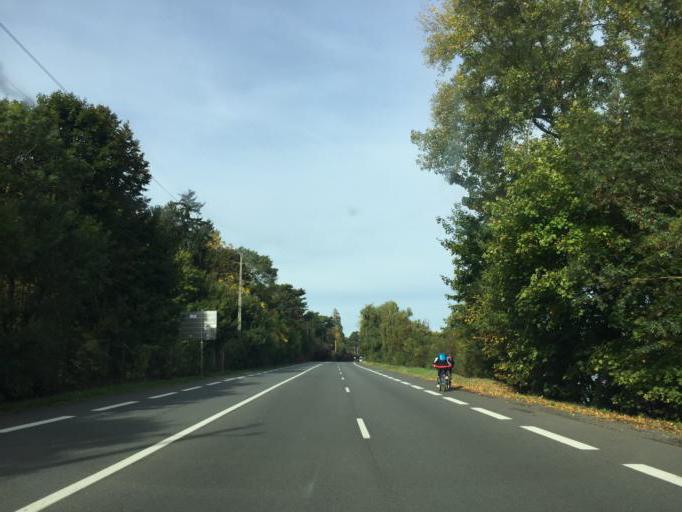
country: FR
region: Rhone-Alpes
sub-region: Departement du Rhone
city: Albigny-sur-Saone
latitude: 45.8807
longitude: 4.8192
